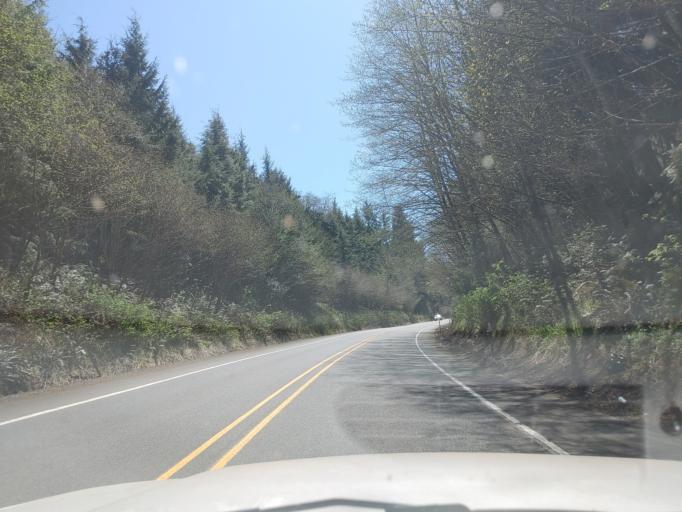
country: US
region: Oregon
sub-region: Clatsop County
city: Warrenton
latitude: 46.1514
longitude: -123.9016
